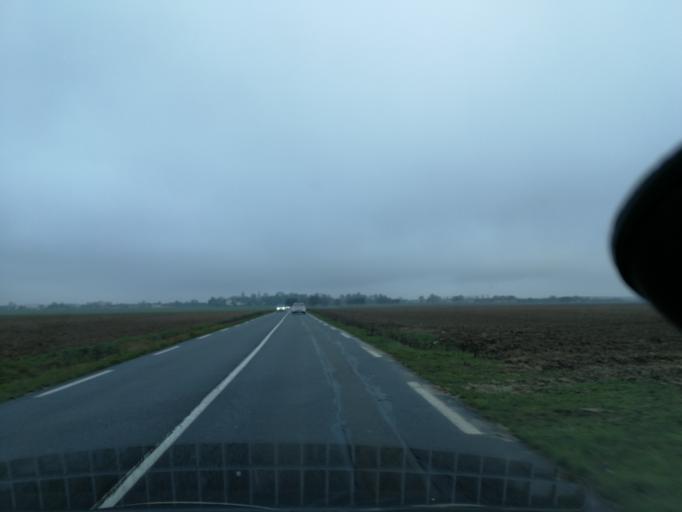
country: FR
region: Ile-de-France
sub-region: Departement de l'Essonne
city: Villiers-le-Bacle
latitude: 48.7360
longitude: 2.1065
